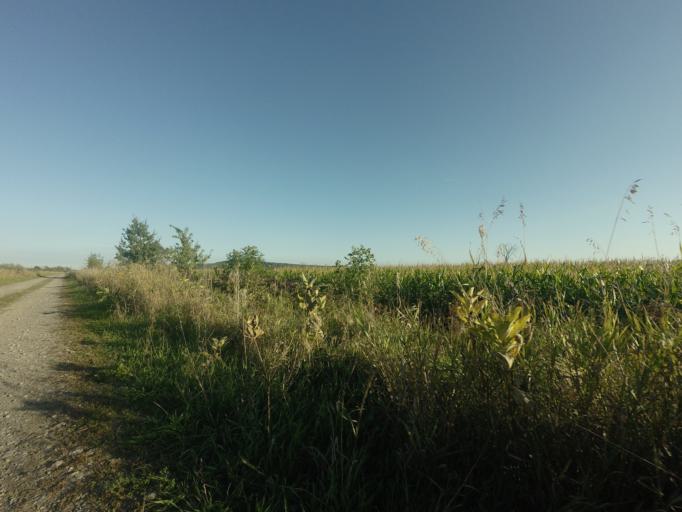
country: CA
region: Quebec
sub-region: Monteregie
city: Rigaud
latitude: 45.4870
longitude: -74.3666
